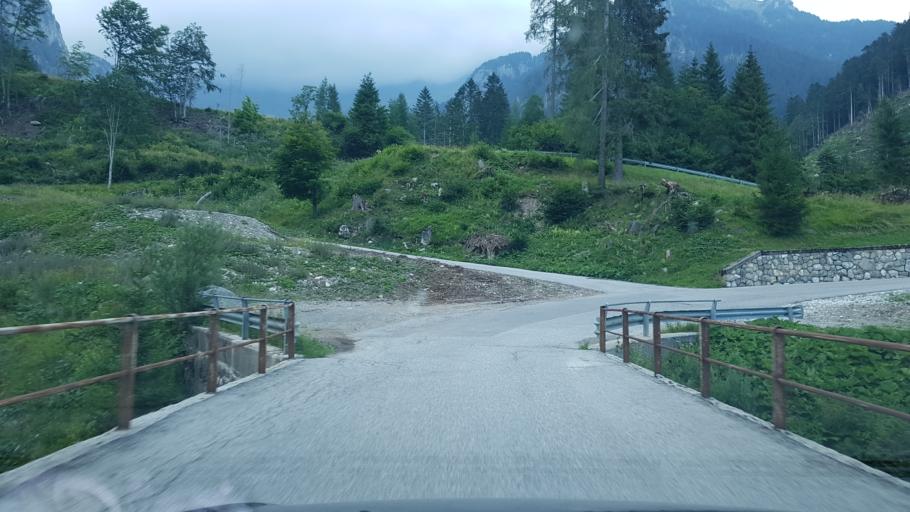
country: IT
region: Friuli Venezia Giulia
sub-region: Provincia di Udine
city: Forni Avoltri
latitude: 46.6064
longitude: 12.7783
